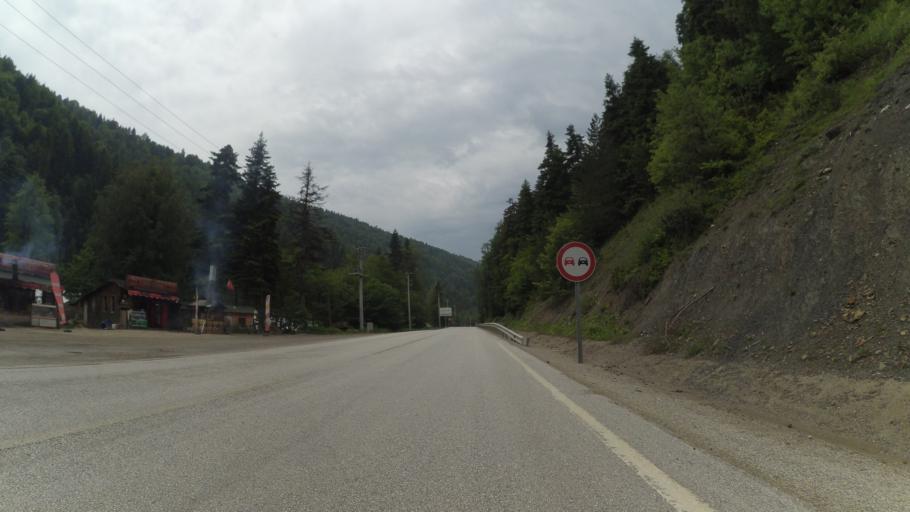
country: TR
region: Duzce
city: Kaynasli
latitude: 40.6413
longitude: 31.3514
